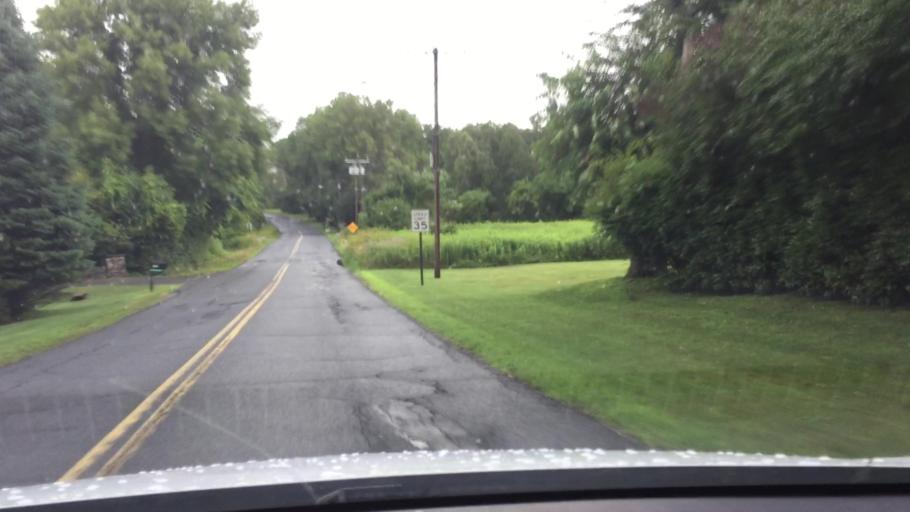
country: US
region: Massachusetts
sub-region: Berkshire County
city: Dalton
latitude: 42.4259
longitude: -73.1938
